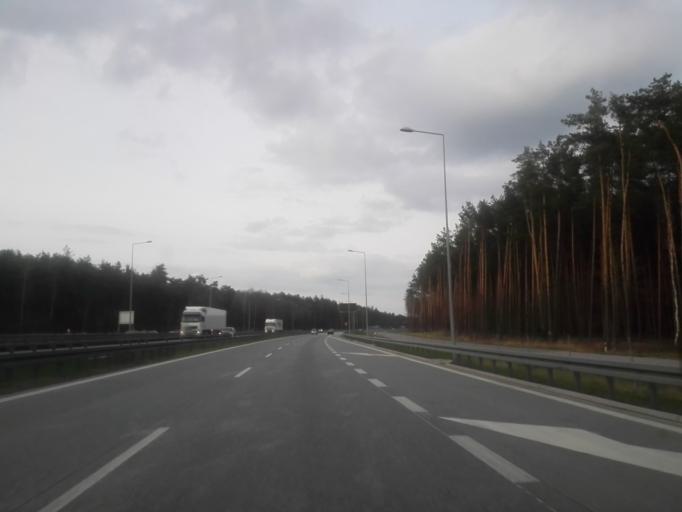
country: PL
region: Lodz Voivodeship
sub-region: Powiat tomaszowski
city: Lubochnia
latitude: 51.6264
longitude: 20.0981
